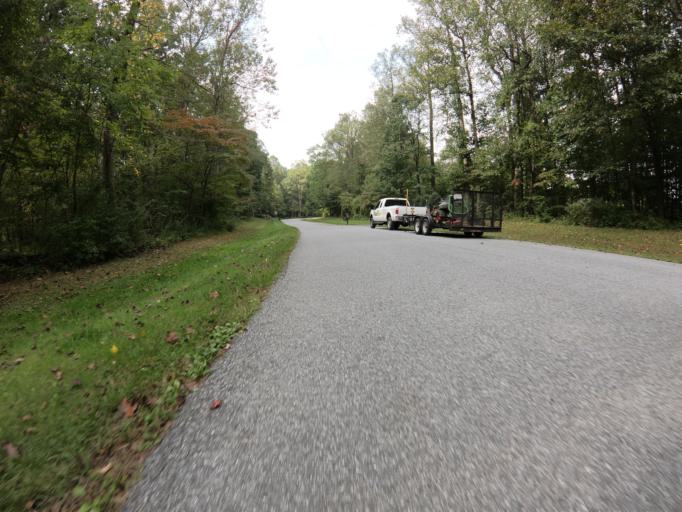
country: US
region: Maryland
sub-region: Howard County
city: Columbia
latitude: 39.2589
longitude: -76.8782
